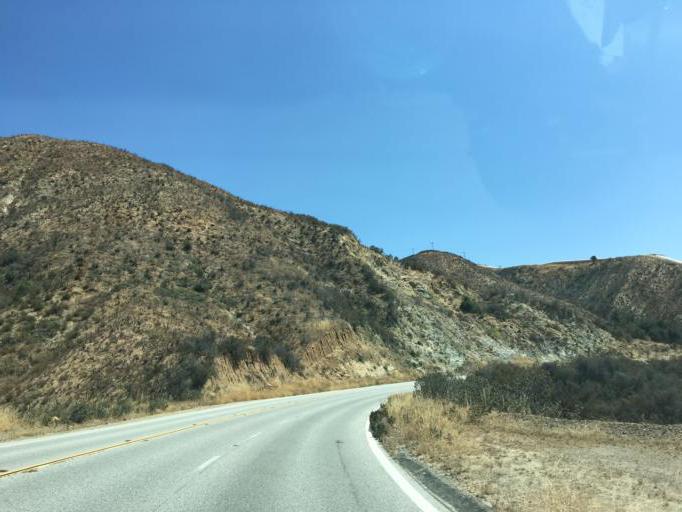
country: US
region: California
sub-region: Los Angeles County
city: Green Valley
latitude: 34.5929
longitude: -118.4593
